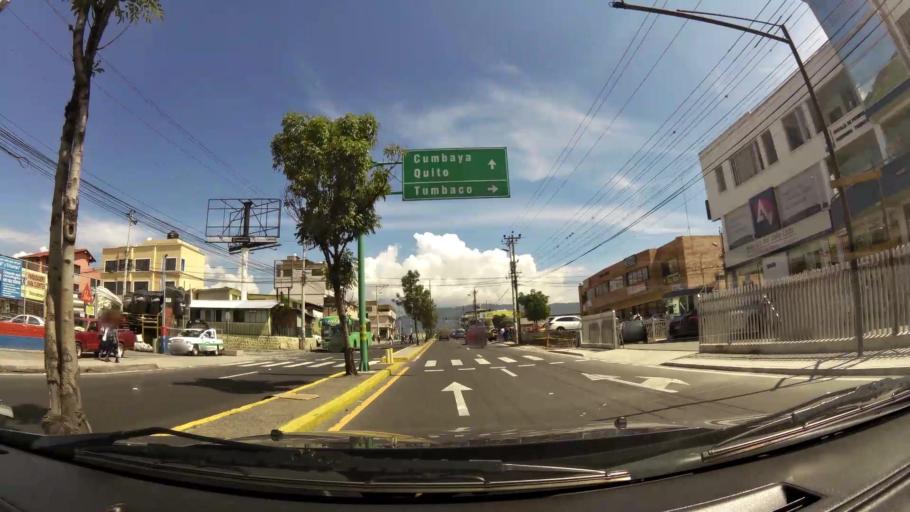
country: EC
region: Pichincha
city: Quito
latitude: -0.2160
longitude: -78.4039
